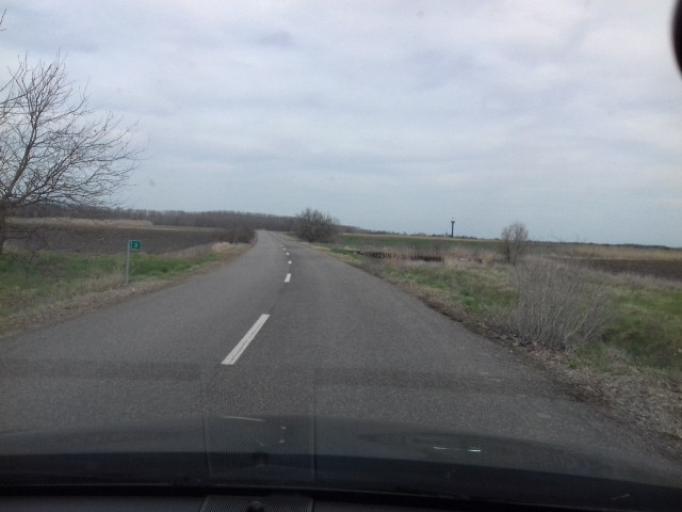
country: HU
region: Bacs-Kiskun
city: Tiszakecske
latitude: 46.8940
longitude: 20.1321
